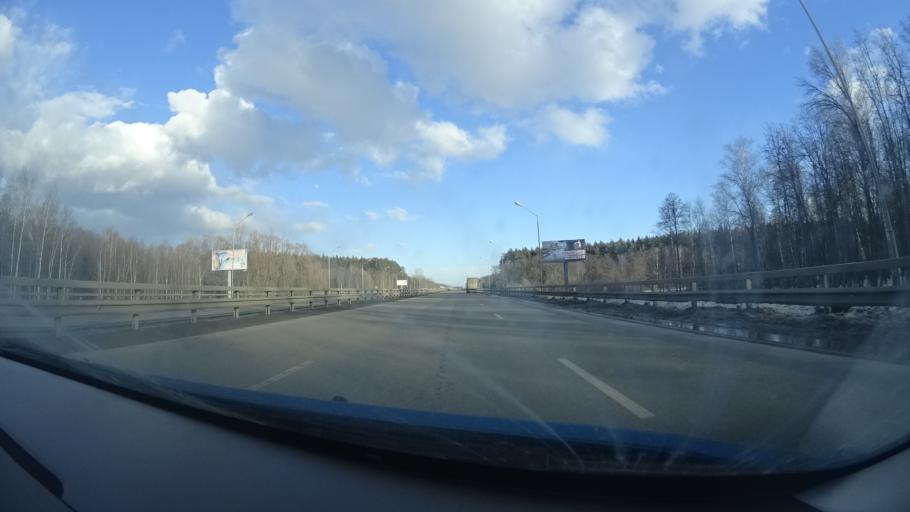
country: RU
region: Bashkortostan
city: Avdon
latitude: 54.6718
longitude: 55.8313
